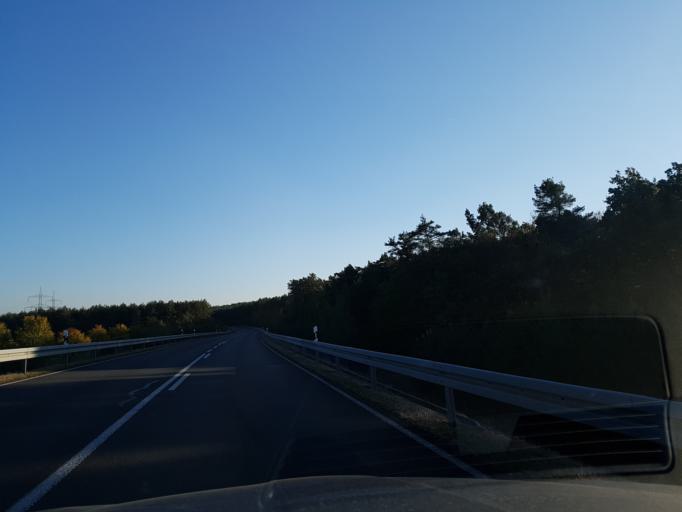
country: DE
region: Brandenburg
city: Bad Liebenwerda
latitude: 51.5267
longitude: 13.4214
